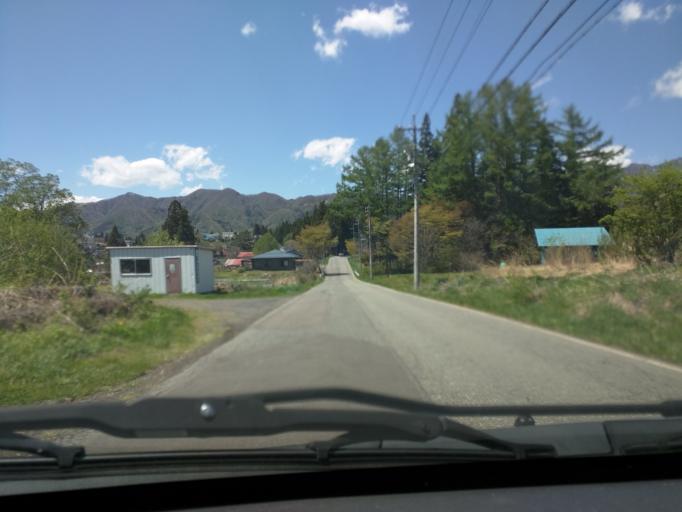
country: JP
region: Nagano
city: Nagano-shi
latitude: 36.7031
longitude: 138.0995
